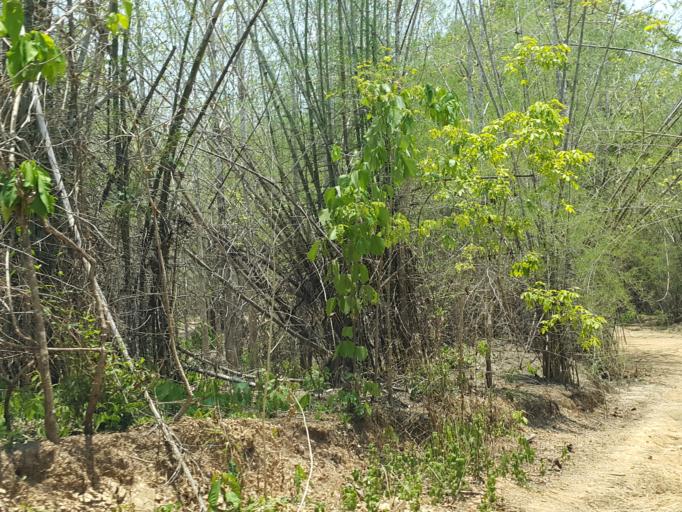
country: TH
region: Kanchanaburi
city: Sai Yok
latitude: 14.2340
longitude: 98.8595
